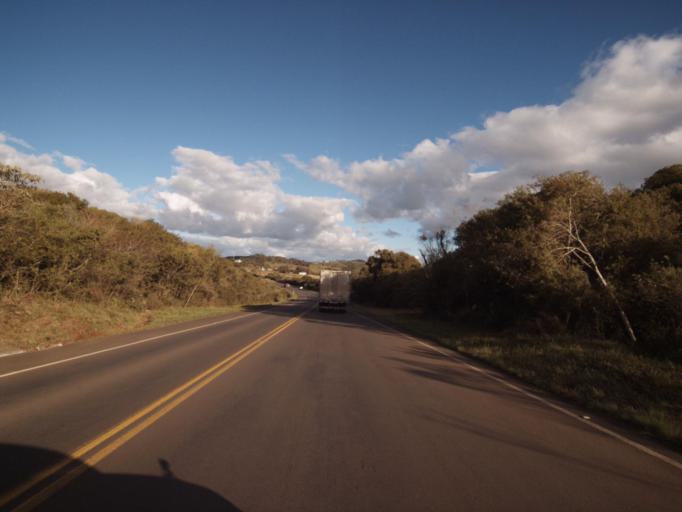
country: BR
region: Santa Catarina
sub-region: Campos Novos
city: Campos Novos
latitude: -27.3422
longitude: -51.3408
